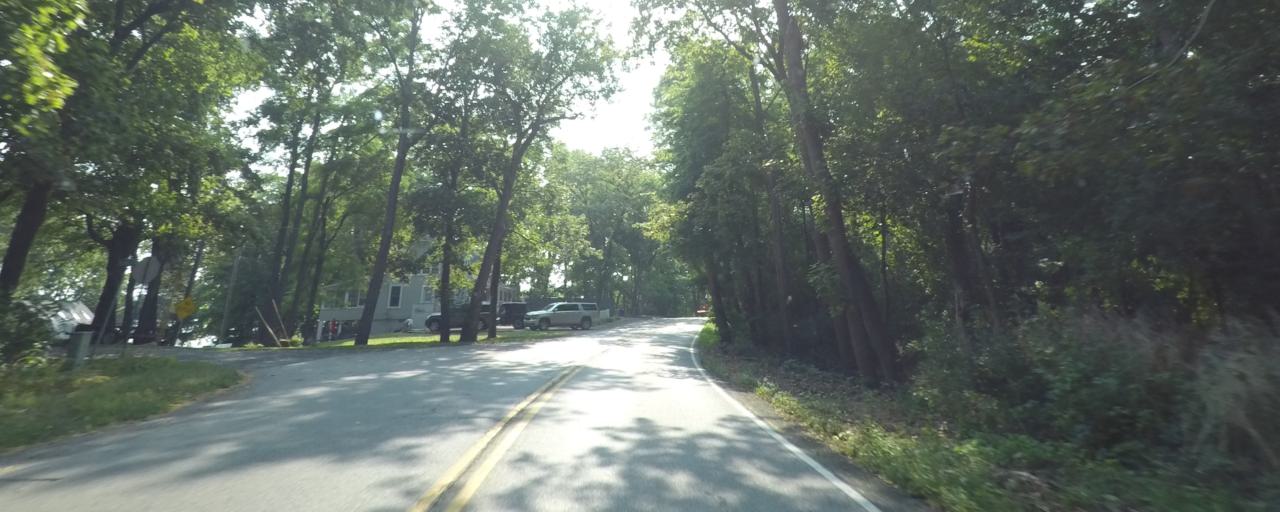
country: US
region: Wisconsin
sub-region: Waukesha County
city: Delafield
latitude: 43.0616
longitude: -88.4387
